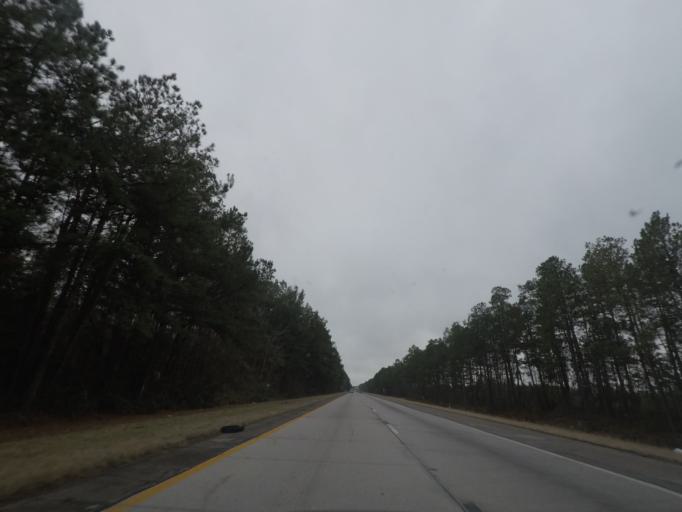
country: US
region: South Carolina
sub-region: Dorchester County
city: Saint George
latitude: 33.0673
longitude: -80.6611
